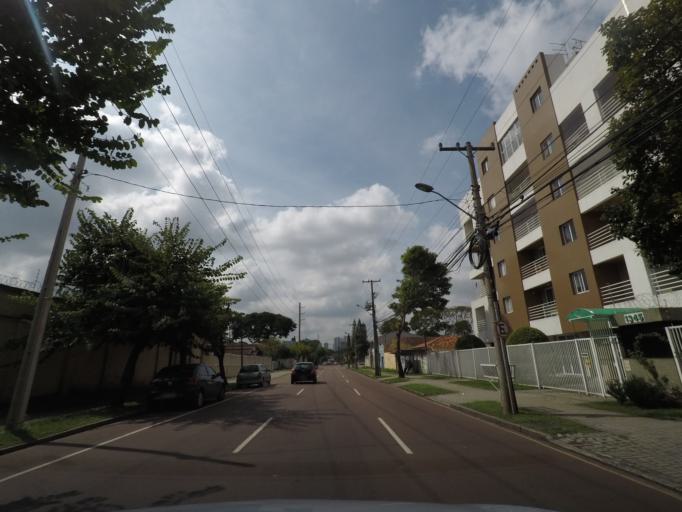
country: BR
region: Parana
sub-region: Curitiba
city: Curitiba
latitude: -25.4428
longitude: -49.2579
